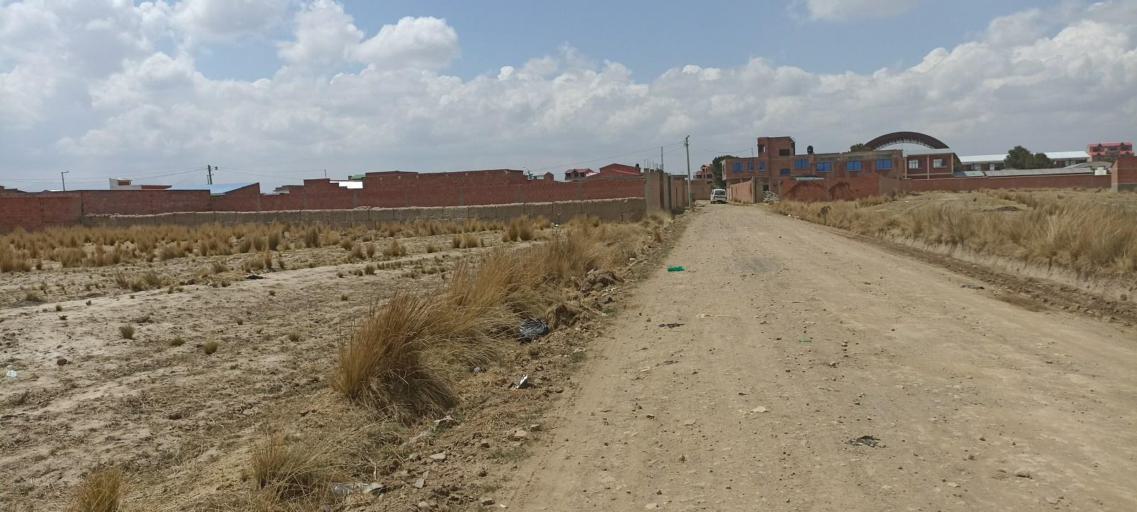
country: BO
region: La Paz
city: Batallas
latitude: -16.4089
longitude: -68.5441
